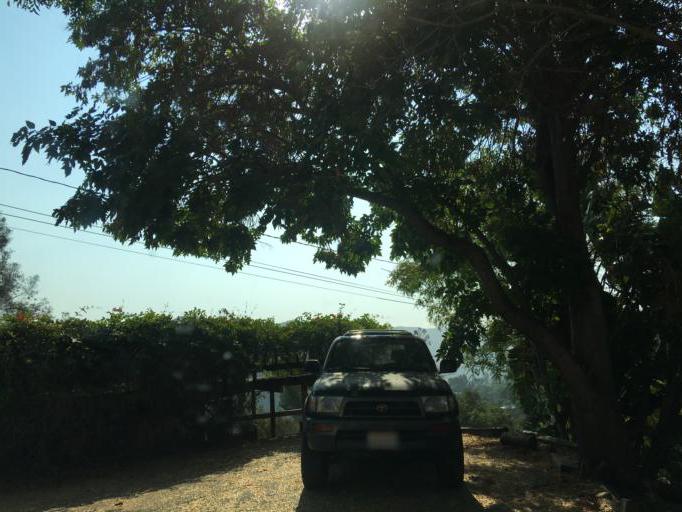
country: US
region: California
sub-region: Los Angeles County
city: Topanga
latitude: 34.0818
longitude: -118.6049
